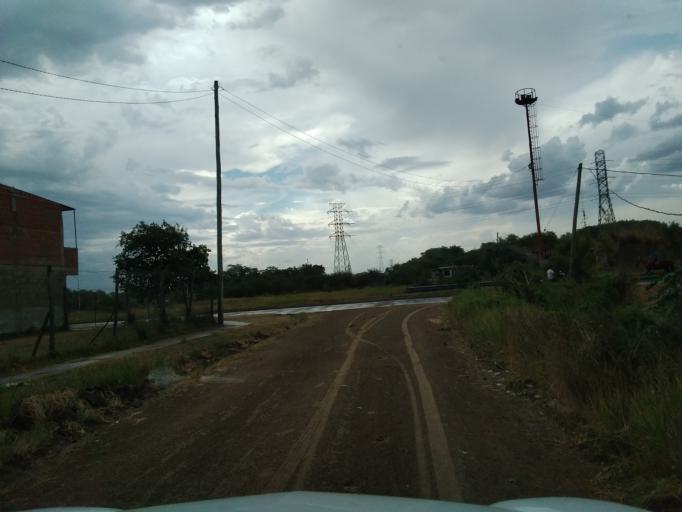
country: AR
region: Corrientes
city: Corrientes
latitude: -27.5175
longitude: -58.7887
